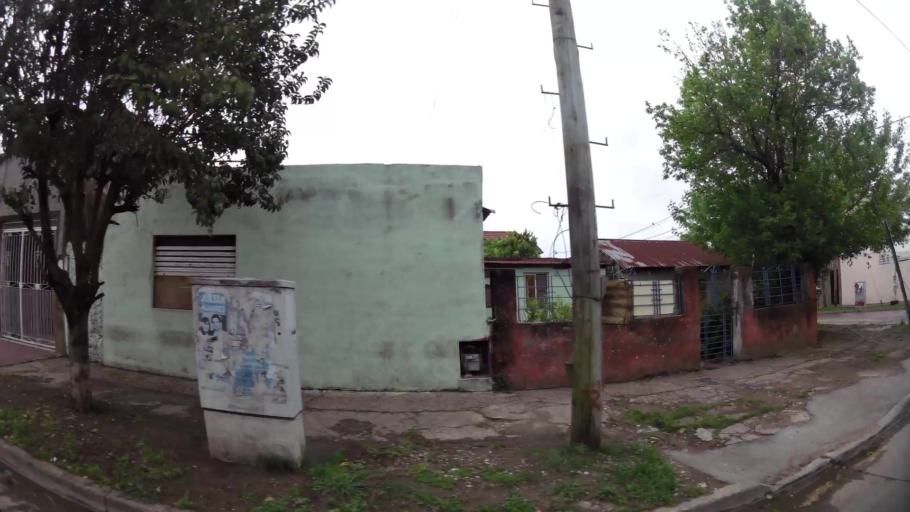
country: AR
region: Buenos Aires
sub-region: Partido de Lanus
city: Lanus
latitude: -34.7357
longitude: -58.3745
